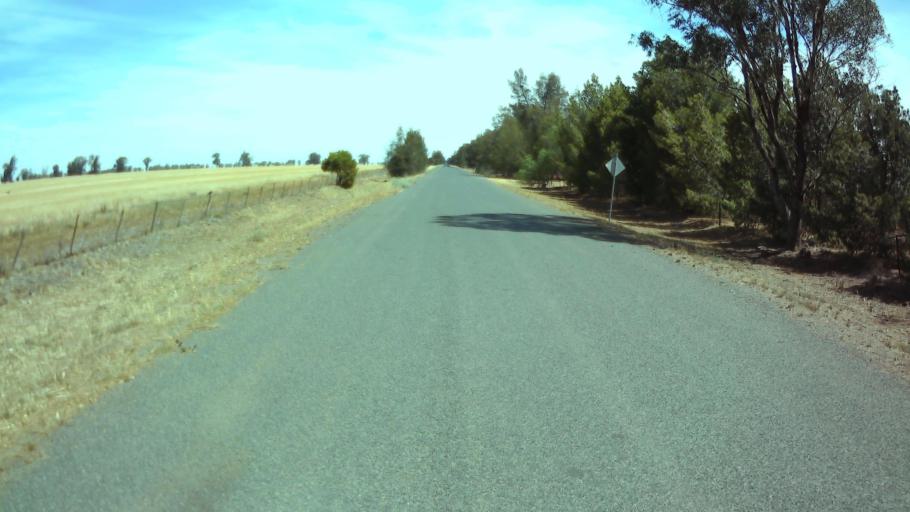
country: AU
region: New South Wales
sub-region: Weddin
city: Grenfell
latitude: -33.9153
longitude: 147.7652
